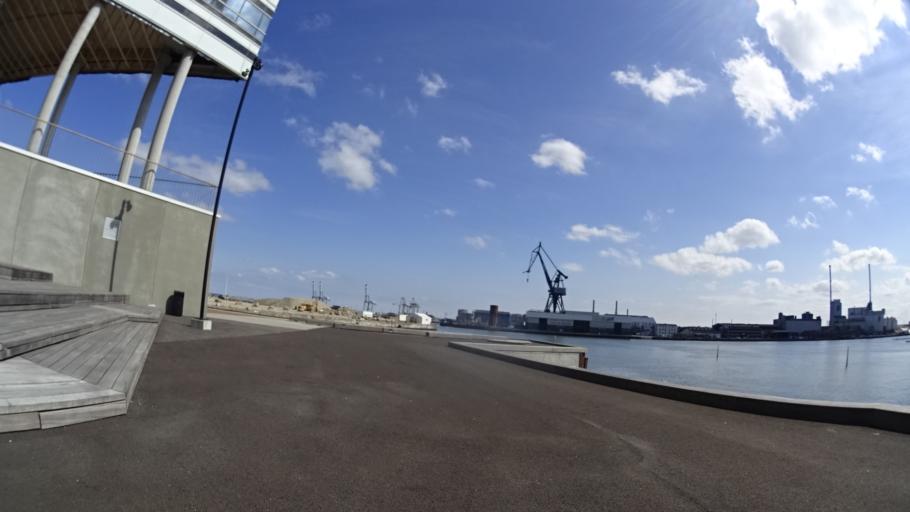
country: DK
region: Central Jutland
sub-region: Arhus Kommune
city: Arhus
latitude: 56.1583
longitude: 10.2160
